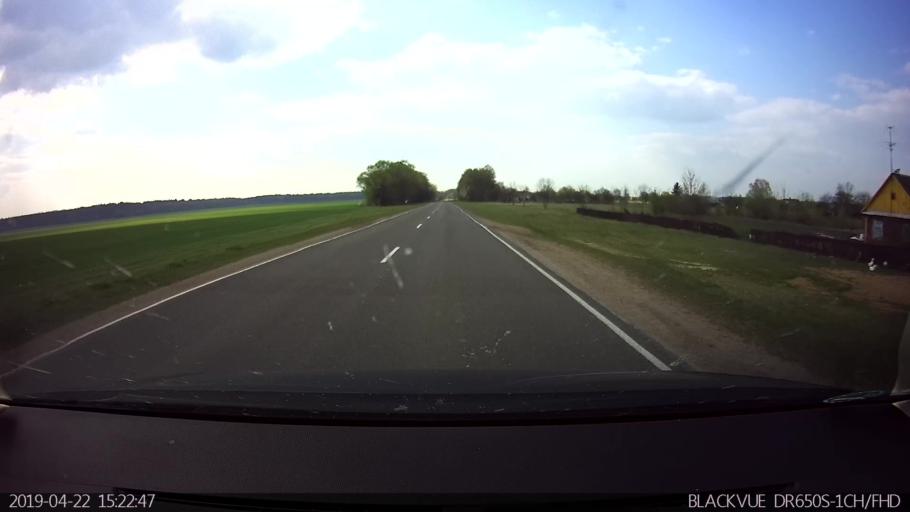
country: BY
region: Brest
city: Vysokaye
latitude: 52.3517
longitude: 23.4390
